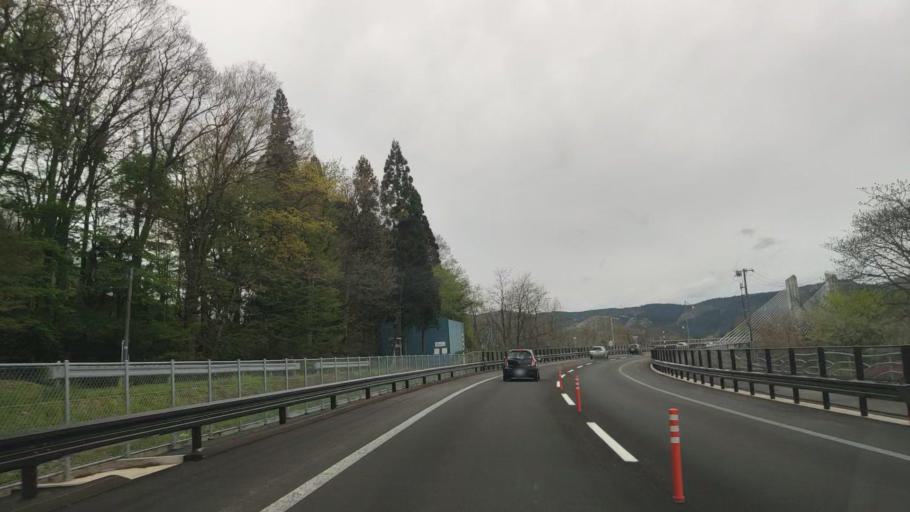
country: JP
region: Akita
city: Takanosu
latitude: 40.2049
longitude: 140.3061
